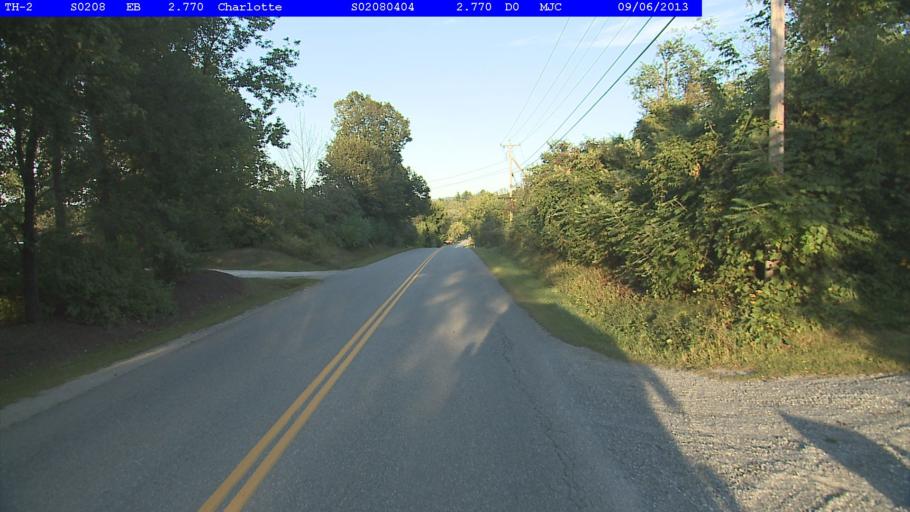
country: US
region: Vermont
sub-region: Chittenden County
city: Hinesburg
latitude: 44.3193
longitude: -73.1931
